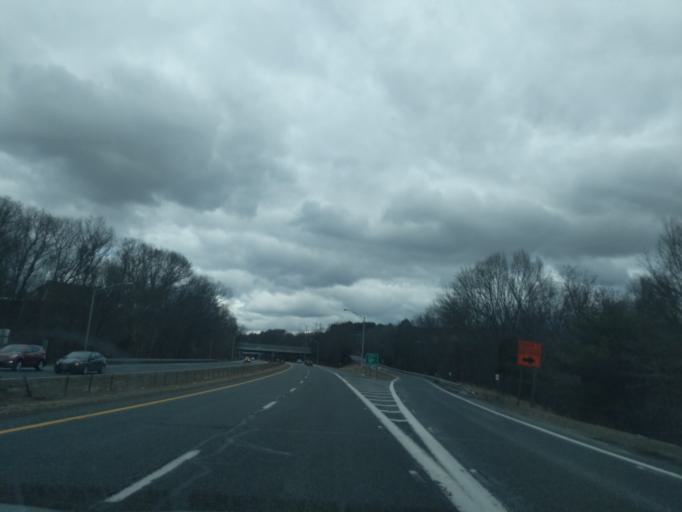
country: US
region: Massachusetts
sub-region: Worcester County
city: Blackstone
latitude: 41.9977
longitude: -71.5572
